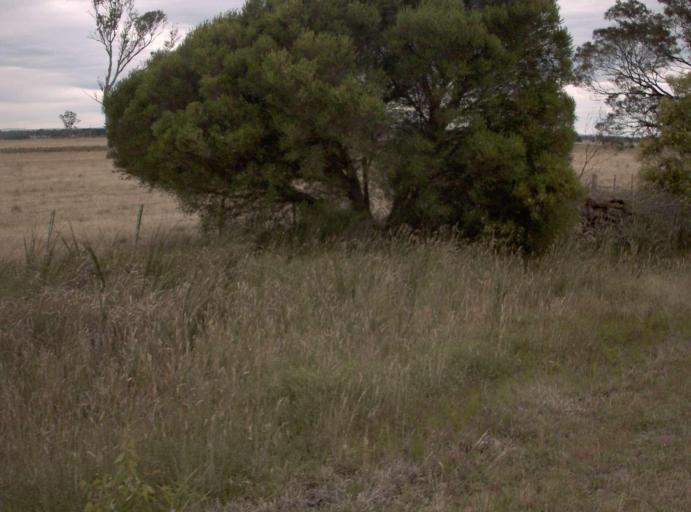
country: AU
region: Victoria
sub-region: East Gippsland
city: Bairnsdale
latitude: -37.9617
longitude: 147.4945
